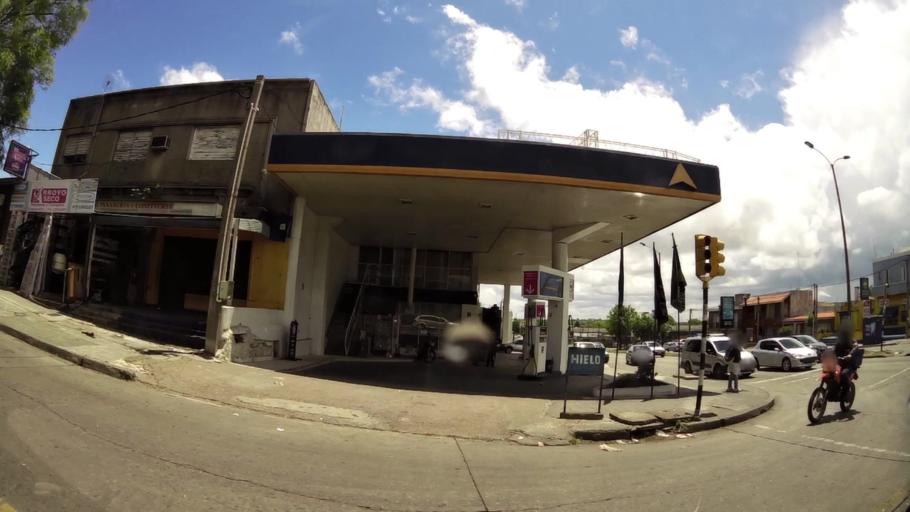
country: UY
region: Montevideo
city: Montevideo
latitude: -34.8534
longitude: -56.1818
